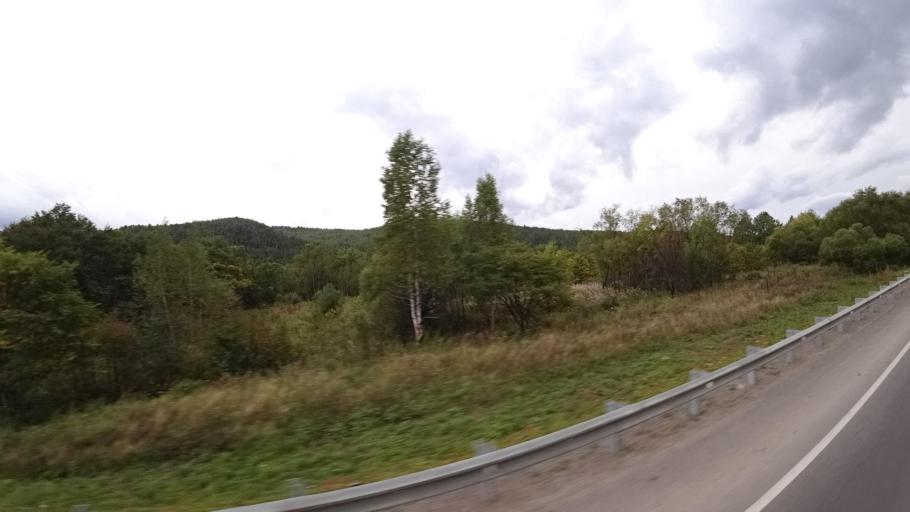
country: RU
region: Jewish Autonomous Oblast
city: Khingansk
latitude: 48.9863
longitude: 131.1374
